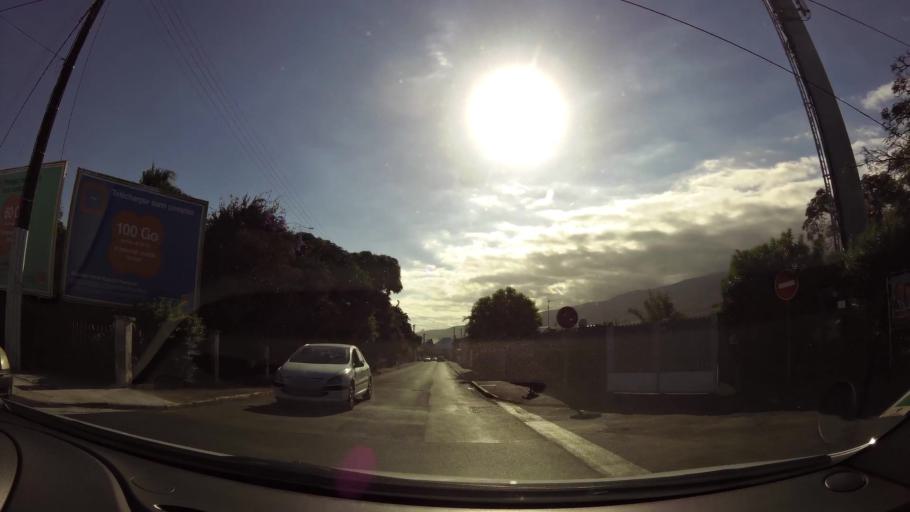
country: RE
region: Reunion
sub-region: Reunion
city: Saint-Louis
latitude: -21.2856
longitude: 55.4125
